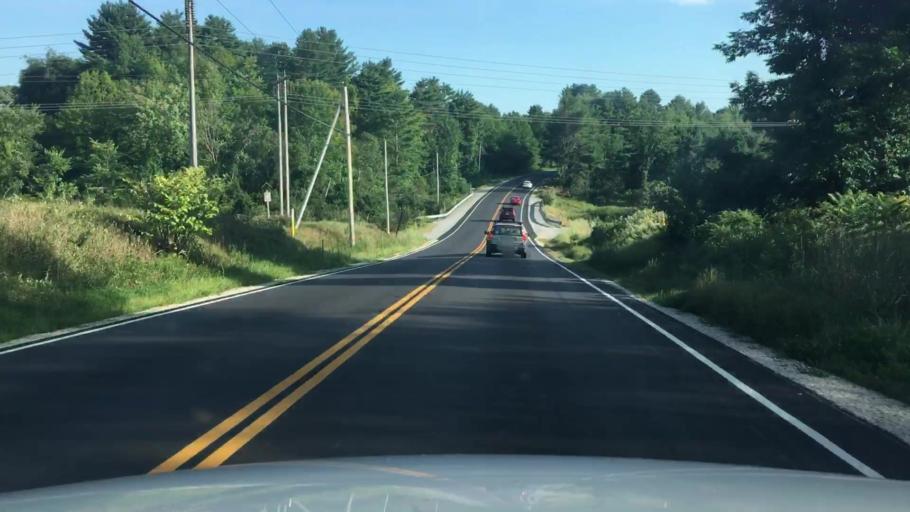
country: US
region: Maine
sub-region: Cumberland County
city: Cumberland Center
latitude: 43.8010
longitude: -70.3078
